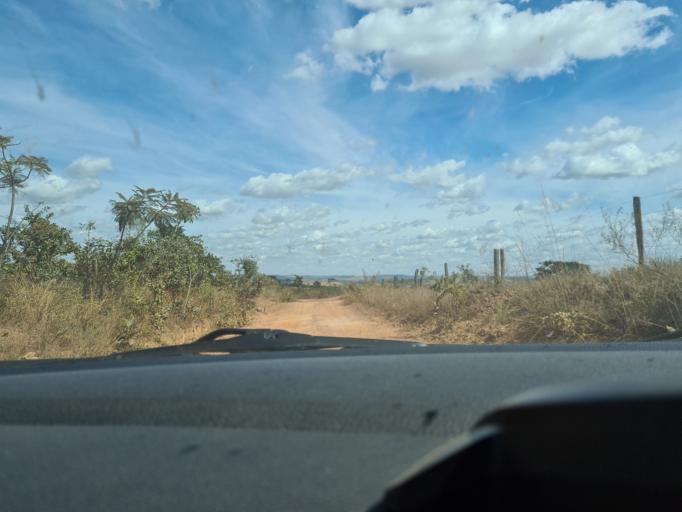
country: BR
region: Goias
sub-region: Silvania
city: Silvania
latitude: -16.5398
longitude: -48.5667
